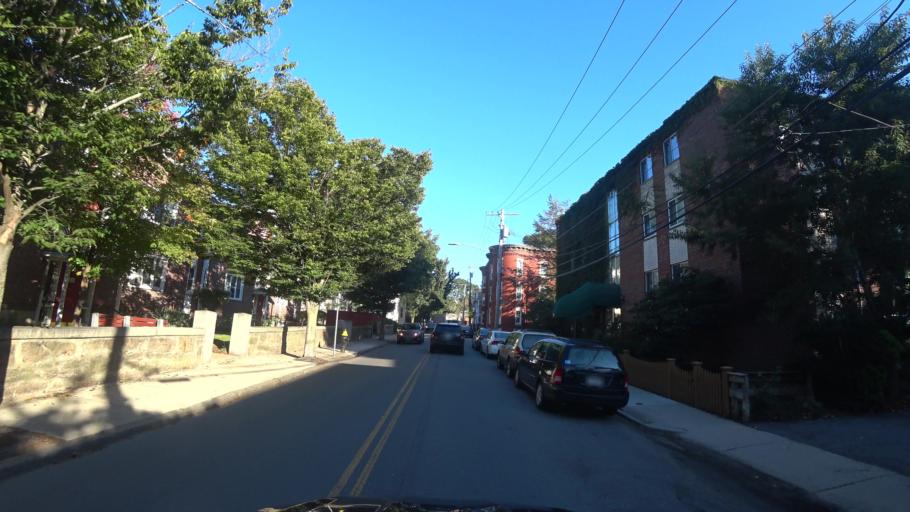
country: US
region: Massachusetts
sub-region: Suffolk County
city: Jamaica Plain
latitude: 42.3151
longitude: -71.1157
